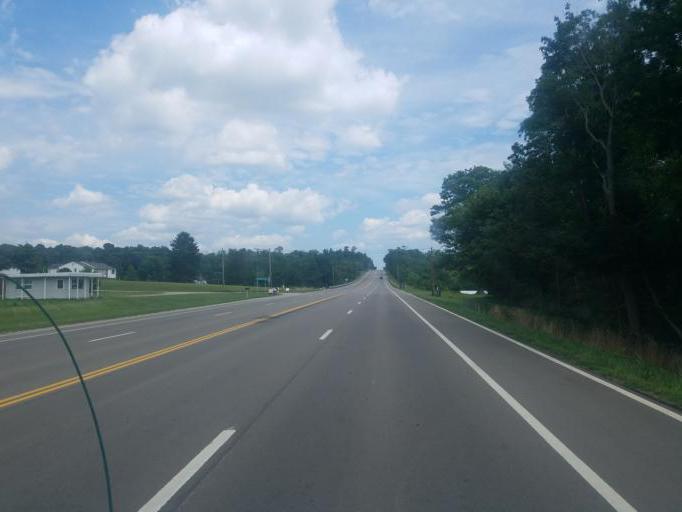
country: US
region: Ohio
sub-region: Muskingum County
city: Frazeysburg
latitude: 39.9561
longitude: -82.1904
